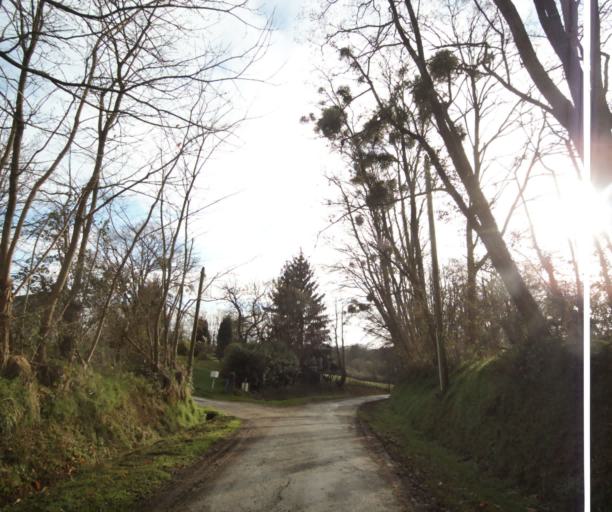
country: FR
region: Pays de la Loire
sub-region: Departement de la Sarthe
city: La Chapelle-Saint-Aubin
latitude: 48.0250
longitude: 0.1629
